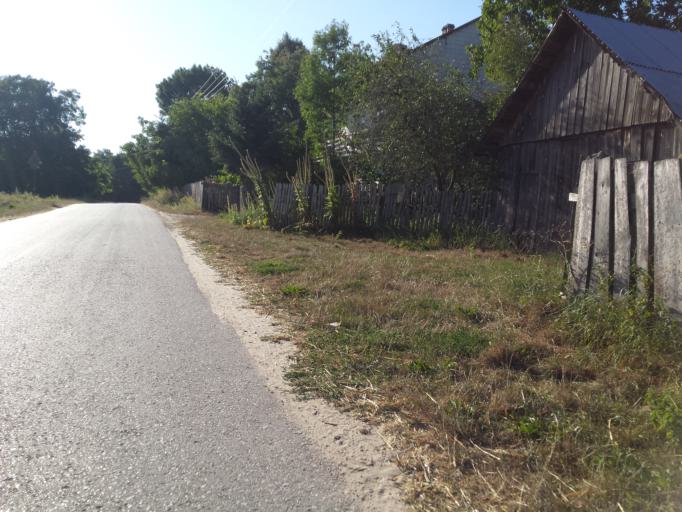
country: PL
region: Swietokrzyskie
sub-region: Powiat kielecki
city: Pierzchnica
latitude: 50.6572
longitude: 20.7878
